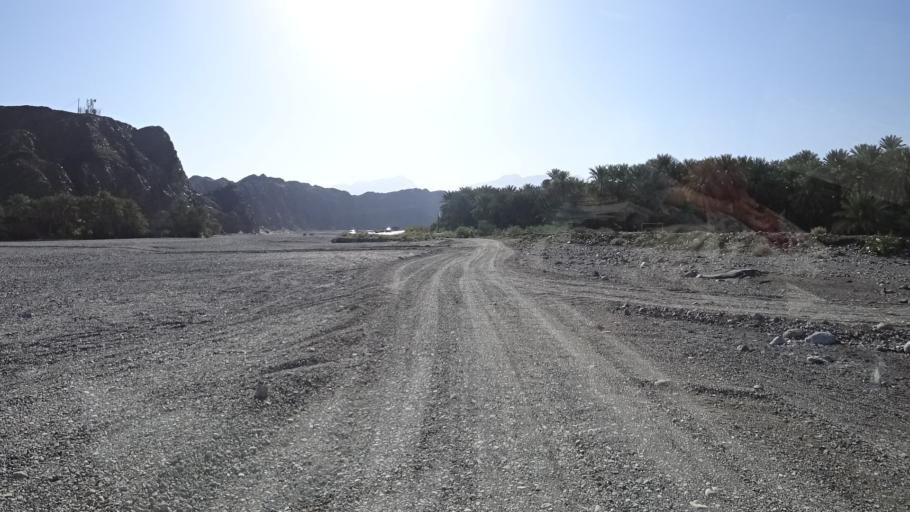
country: OM
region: Al Batinah
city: Bayt al `Awabi
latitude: 23.3859
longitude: 57.6597
